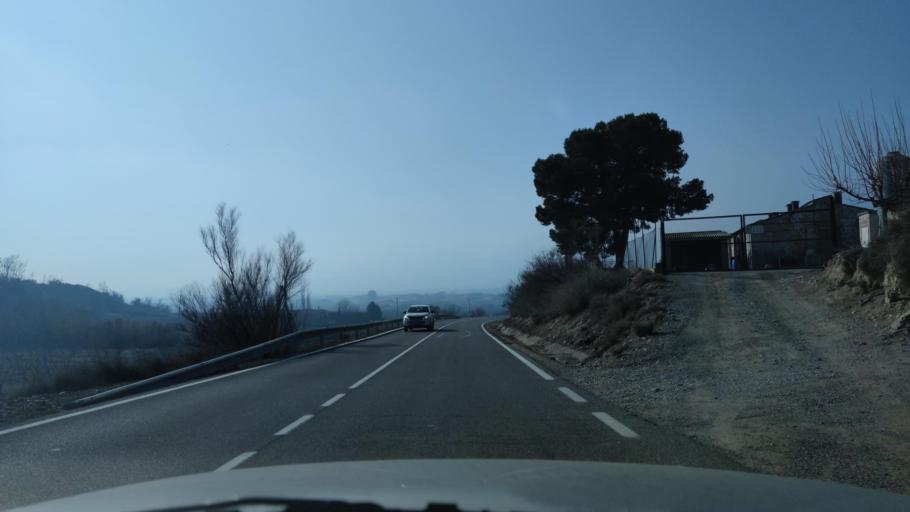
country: ES
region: Catalonia
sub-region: Provincia de Lleida
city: la Granja d'Escarp
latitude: 41.4619
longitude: 0.3675
